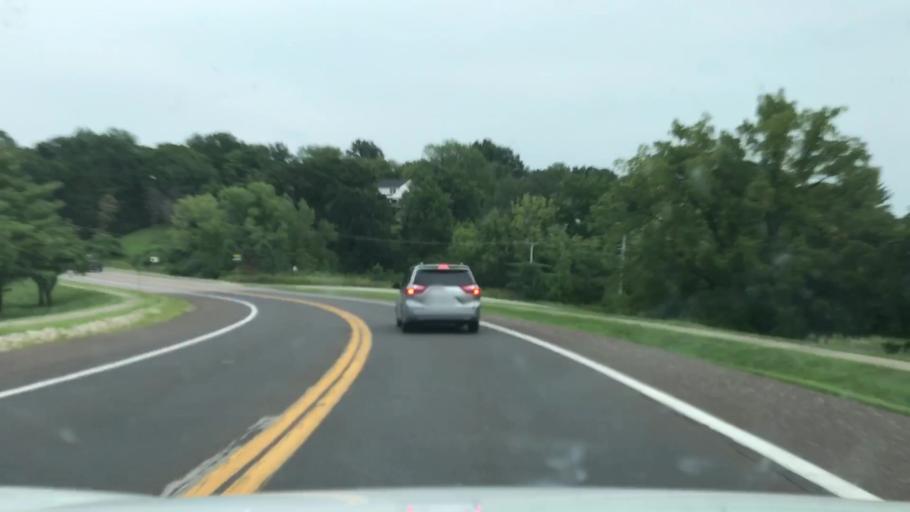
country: US
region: Missouri
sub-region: Saint Louis County
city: Clarkson Valley
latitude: 38.6243
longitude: -90.5906
